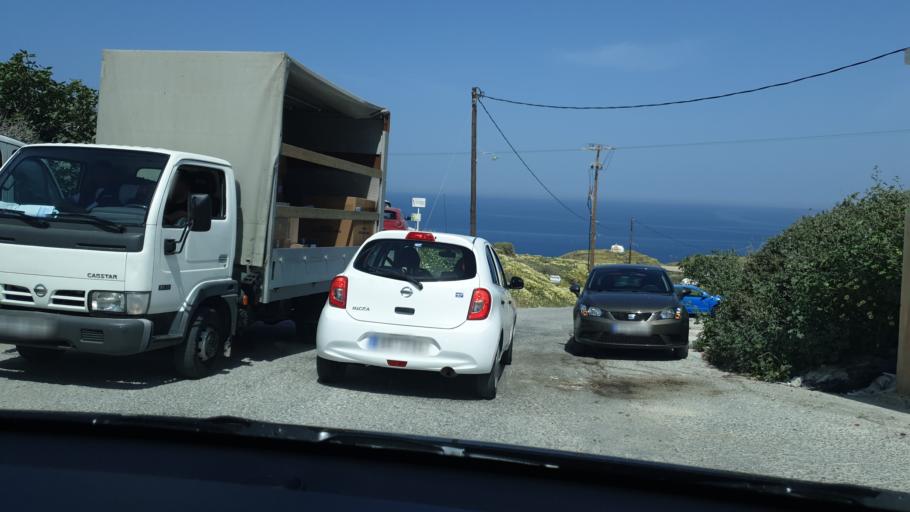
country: GR
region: South Aegean
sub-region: Nomos Kykladon
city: Oia
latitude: 36.4626
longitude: 25.3731
